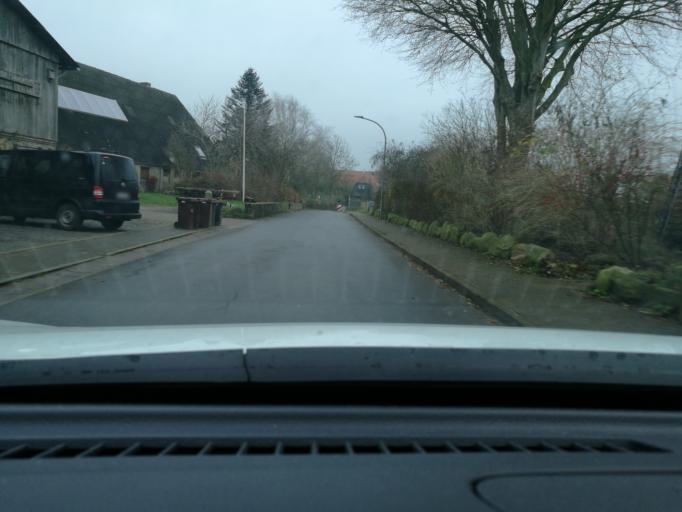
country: DE
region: Schleswig-Holstein
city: Holzbunge
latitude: 54.3811
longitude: 9.7032
